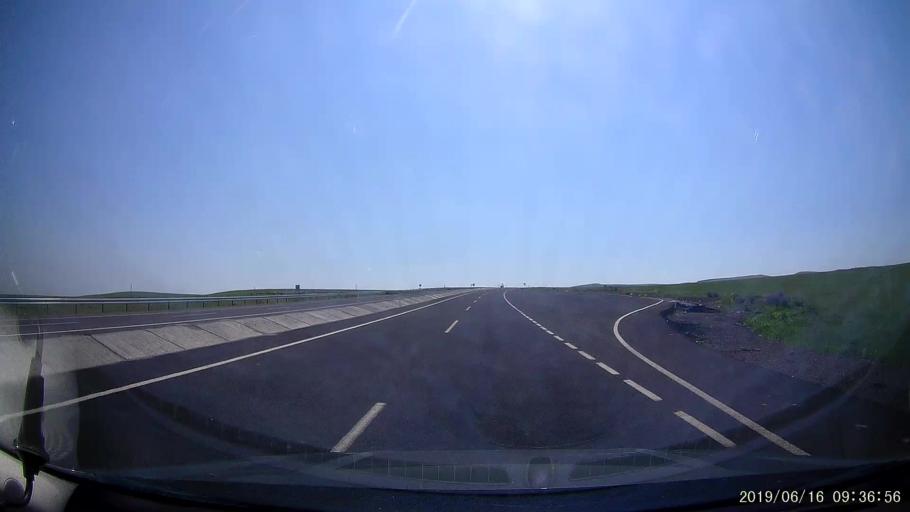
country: TR
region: Kars
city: Kars
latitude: 40.5554
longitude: 43.1832
